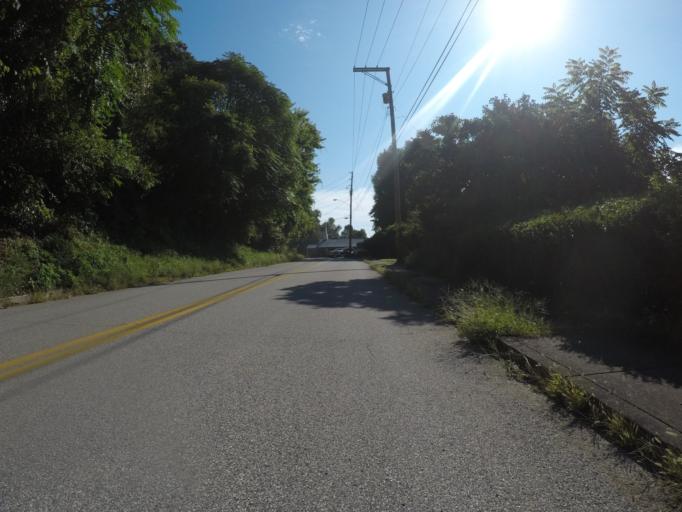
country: US
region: Kentucky
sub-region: Boyd County
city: Ashland
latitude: 38.4551
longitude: -82.6171
